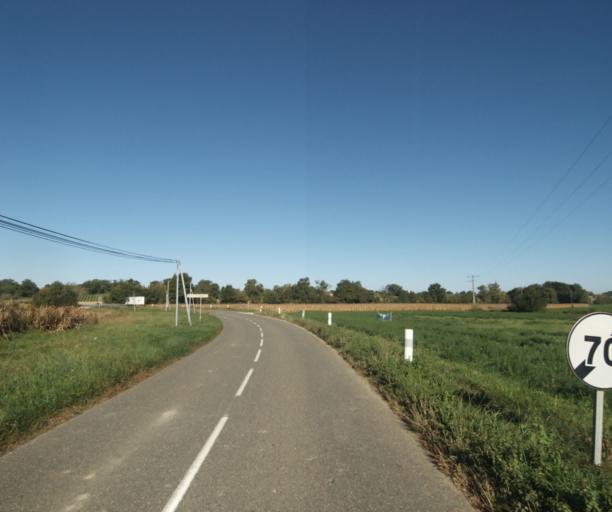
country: FR
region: Midi-Pyrenees
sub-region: Departement du Gers
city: Gondrin
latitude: 43.8154
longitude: 0.1861
